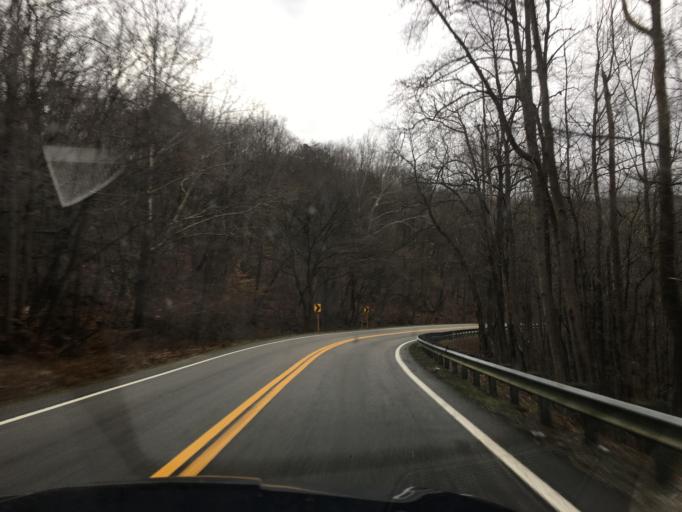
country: US
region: Tennessee
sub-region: Cumberland County
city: Lake Tansi
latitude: 35.8698
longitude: -84.9277
